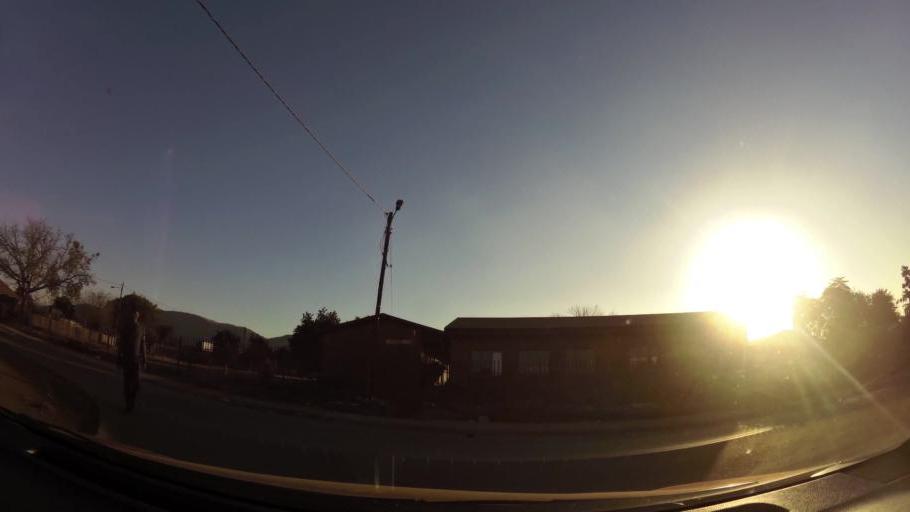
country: ZA
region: North-West
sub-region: Bojanala Platinum District Municipality
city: Rustenburg
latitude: -25.6308
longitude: 27.2116
